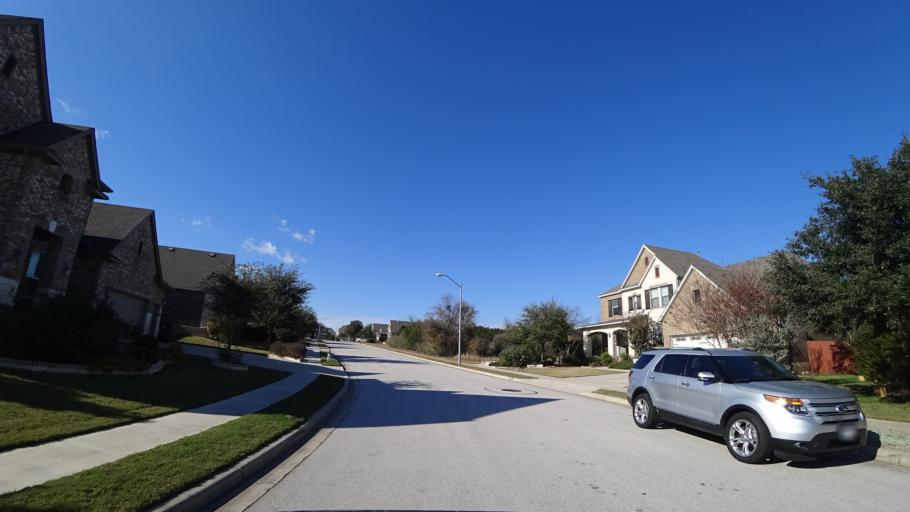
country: US
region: Texas
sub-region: Williamson County
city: Brushy Creek
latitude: 30.4880
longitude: -97.7239
